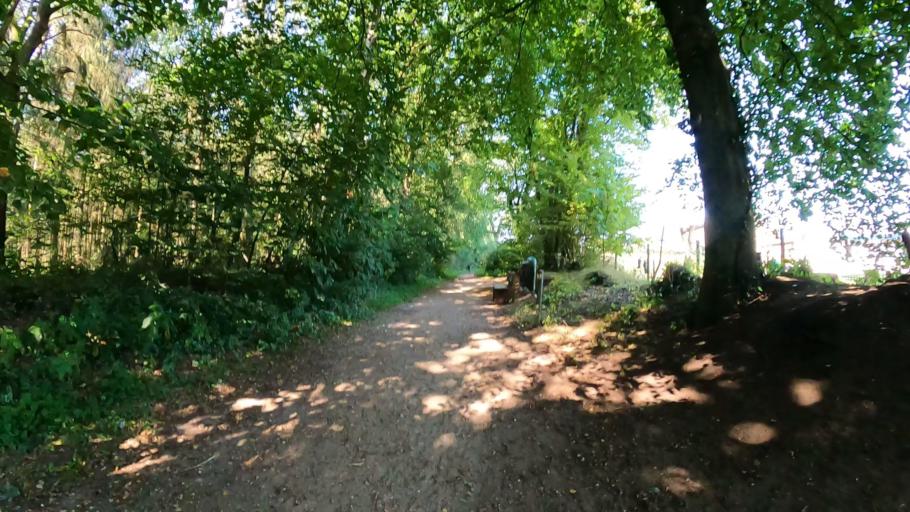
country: DE
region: Schleswig-Holstein
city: Henstedt-Ulzburg
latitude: 53.7651
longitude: 9.9779
